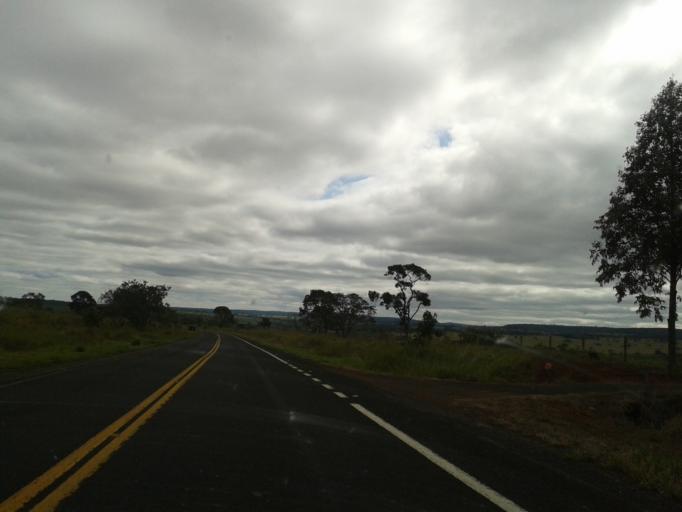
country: BR
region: Minas Gerais
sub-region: Campina Verde
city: Campina Verde
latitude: -19.5173
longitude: -49.6430
